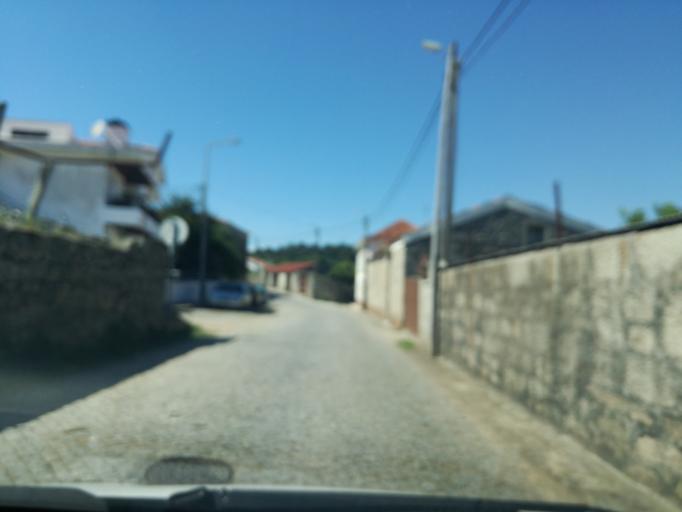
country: PT
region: Porto
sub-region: Maia
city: Maia
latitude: 41.2424
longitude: -8.6127
